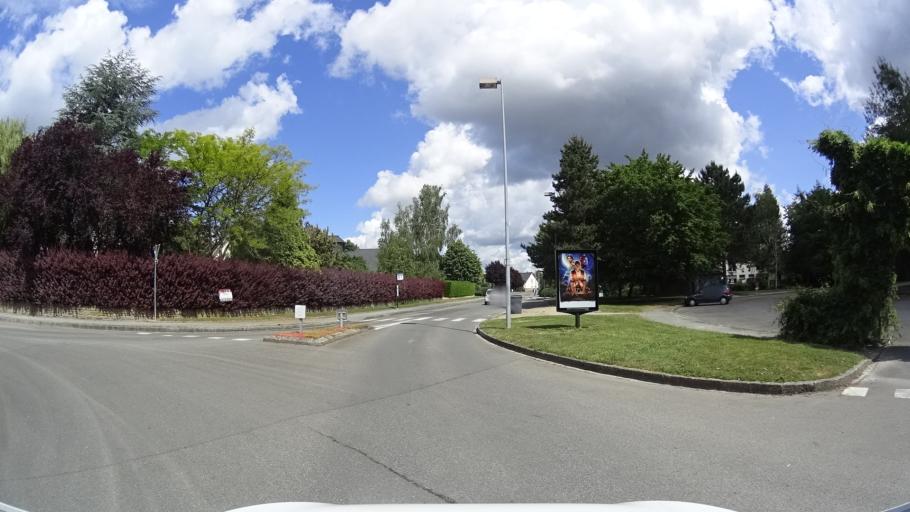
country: FR
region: Brittany
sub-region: Departement d'Ille-et-Vilaine
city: Chartres-de-Bretagne
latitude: 48.0328
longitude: -1.7072
